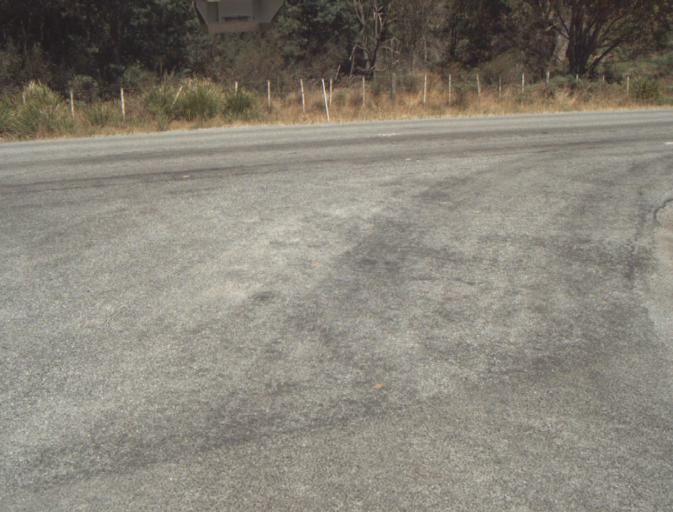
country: AU
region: Tasmania
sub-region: Dorset
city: Scottsdale
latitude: -41.3108
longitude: 147.3704
